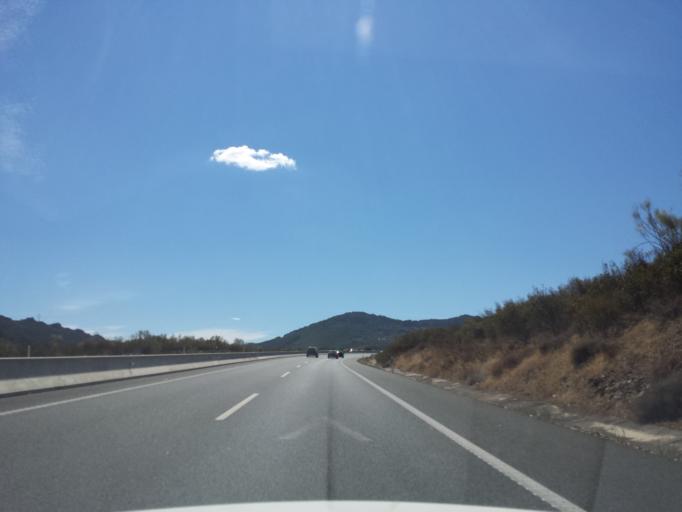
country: ES
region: Extremadura
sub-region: Provincia de Caceres
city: Higuera
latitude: 39.7101
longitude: -5.6934
